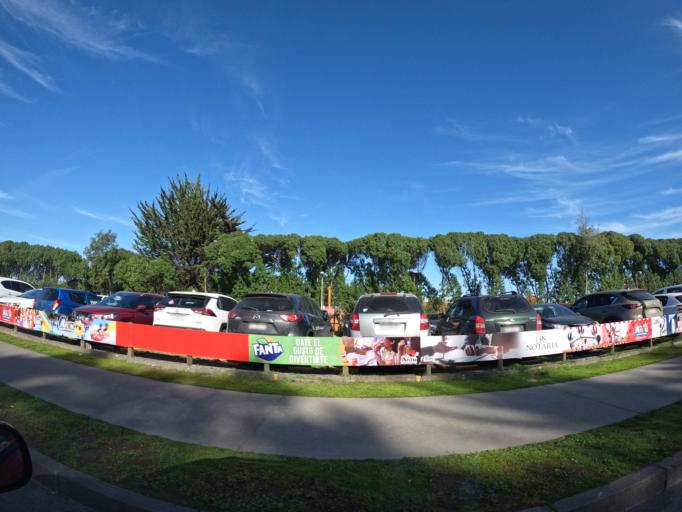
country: CL
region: Biobio
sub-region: Provincia de Concepcion
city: Concepcion
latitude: -36.7763
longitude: -73.0697
